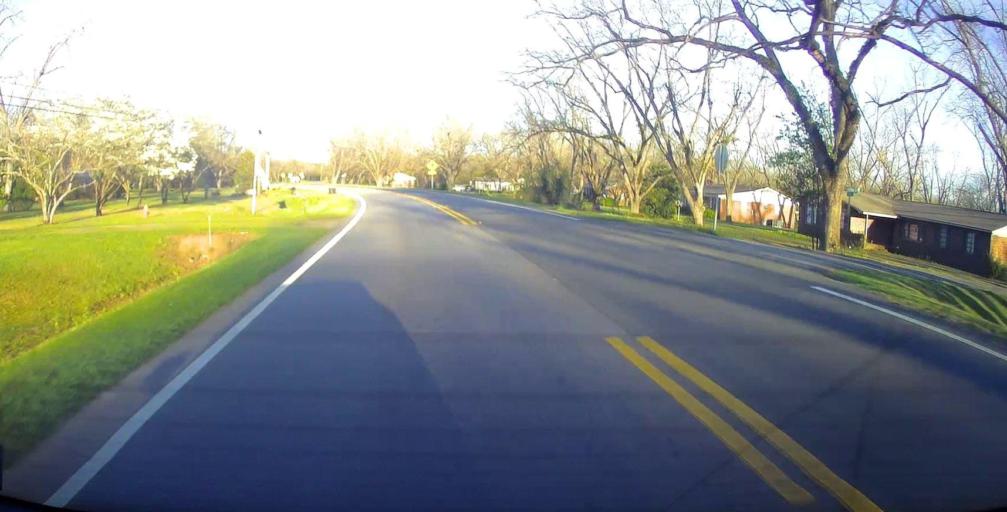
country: US
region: Georgia
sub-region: Wilcox County
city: Rochelle
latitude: 31.9509
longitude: -83.4424
